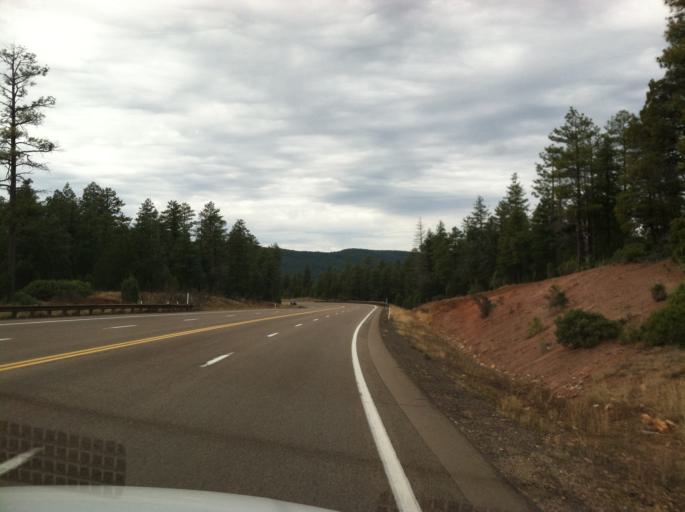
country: US
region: Arizona
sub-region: Gila County
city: Star Valley
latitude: 34.3011
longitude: -110.9582
